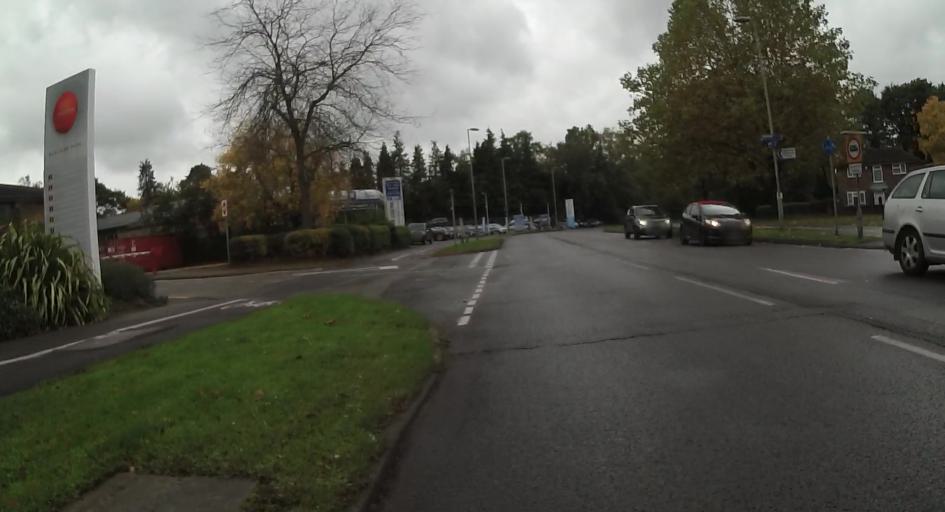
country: GB
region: England
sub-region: Surrey
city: Woking
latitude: 51.3282
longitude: -0.5358
